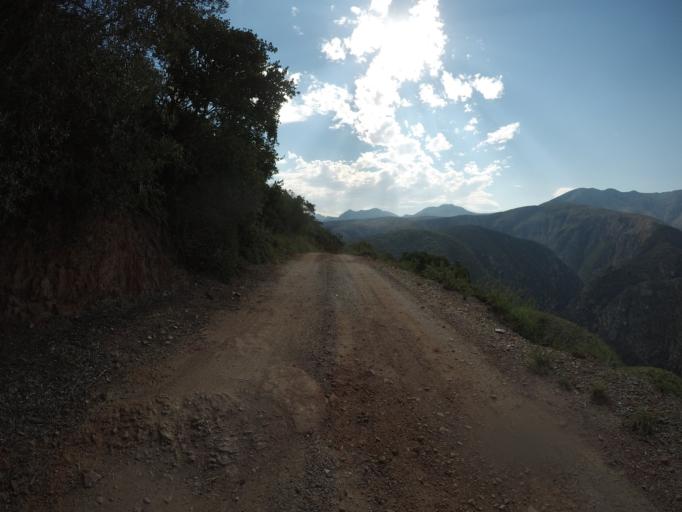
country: ZA
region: Eastern Cape
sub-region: Cacadu District Municipality
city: Kareedouw
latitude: -33.6480
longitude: 24.3472
